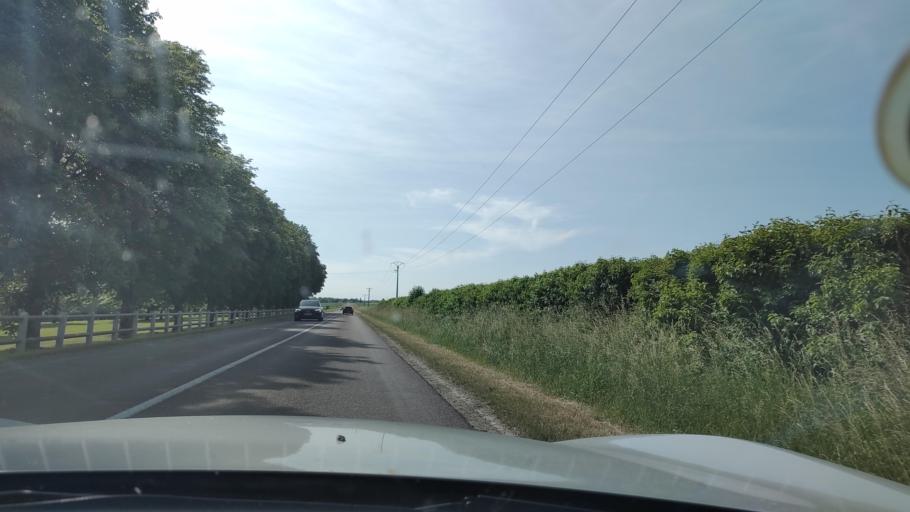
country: FR
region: Champagne-Ardenne
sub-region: Departement de l'Aube
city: Nogent-sur-Seine
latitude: 48.4855
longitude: 3.5333
